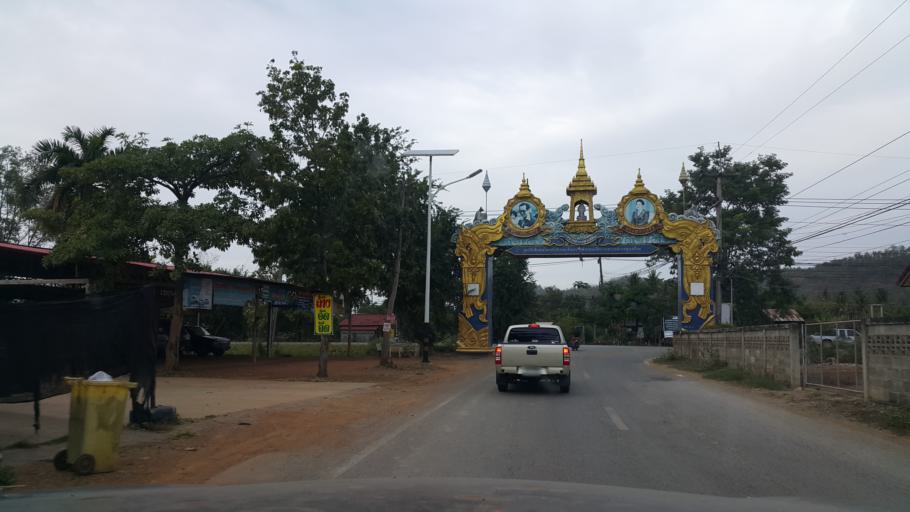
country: TH
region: Sukhothai
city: Thung Saliam
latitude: 17.3364
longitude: 99.5828
